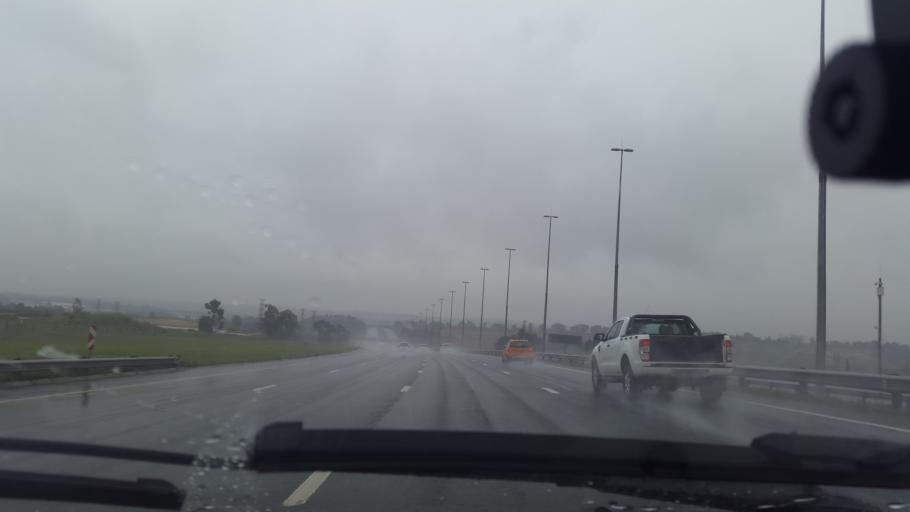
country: ZA
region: Gauteng
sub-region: City of Johannesburg Metropolitan Municipality
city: Johannesburg
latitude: -26.2241
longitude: 27.9613
